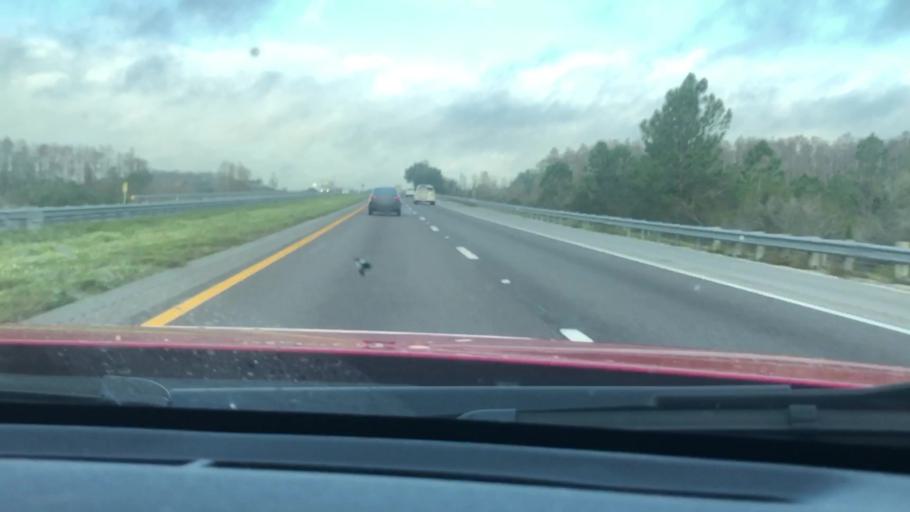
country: US
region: Florida
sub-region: Osceola County
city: Saint Cloud
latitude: 28.0080
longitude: -81.1564
